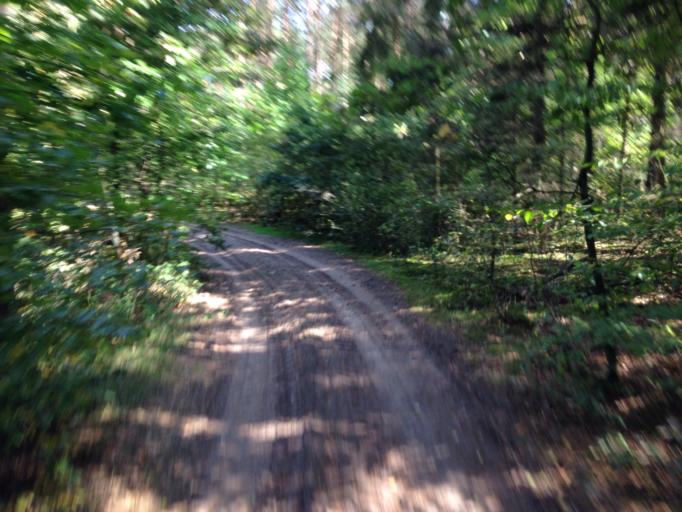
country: PL
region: Warmian-Masurian Voivodeship
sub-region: Powiat dzialdowski
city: Lidzbark
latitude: 53.2071
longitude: 19.7561
